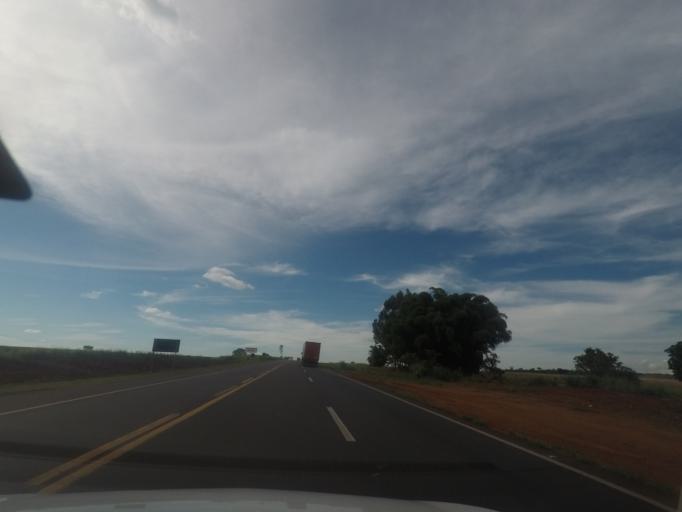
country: BR
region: Minas Gerais
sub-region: Monte Alegre De Minas
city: Monte Alegre de Minas
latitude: -19.0206
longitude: -49.0138
